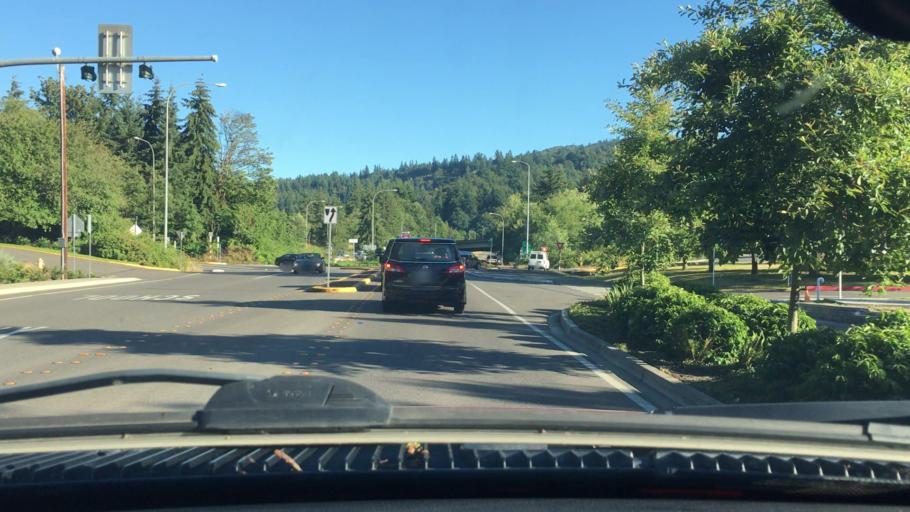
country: US
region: Washington
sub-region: King County
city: West Lake Sammamish
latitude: 47.5686
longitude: -122.1002
